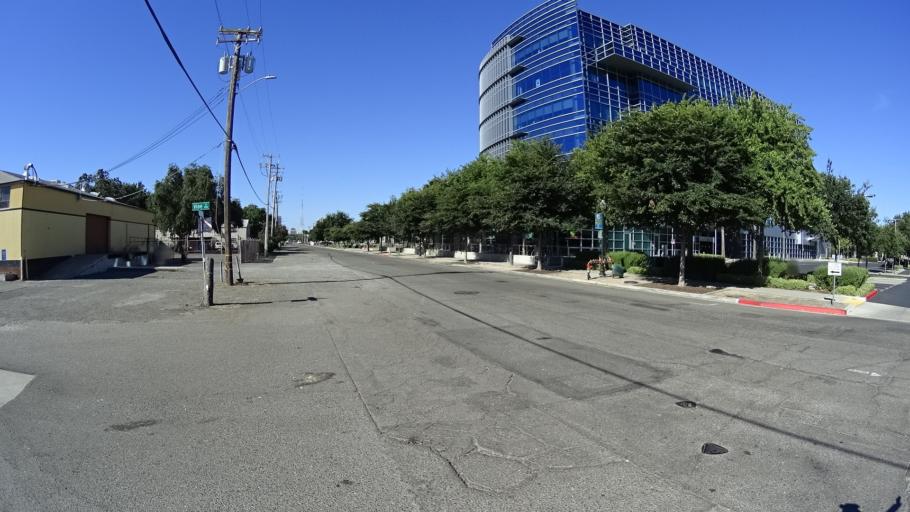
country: US
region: California
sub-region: Sacramento County
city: Sacramento
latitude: 38.5985
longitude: -121.4855
